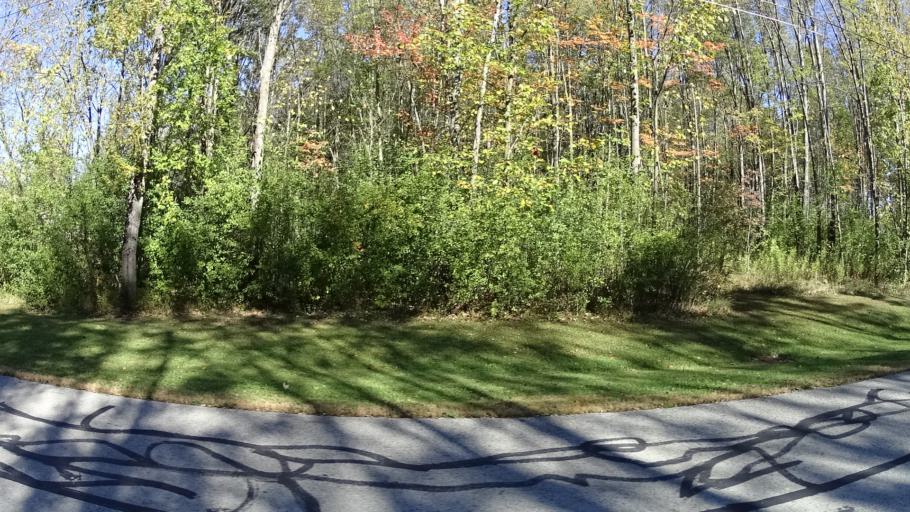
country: US
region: Ohio
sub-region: Lorain County
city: Oberlin
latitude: 41.2972
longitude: -82.1962
